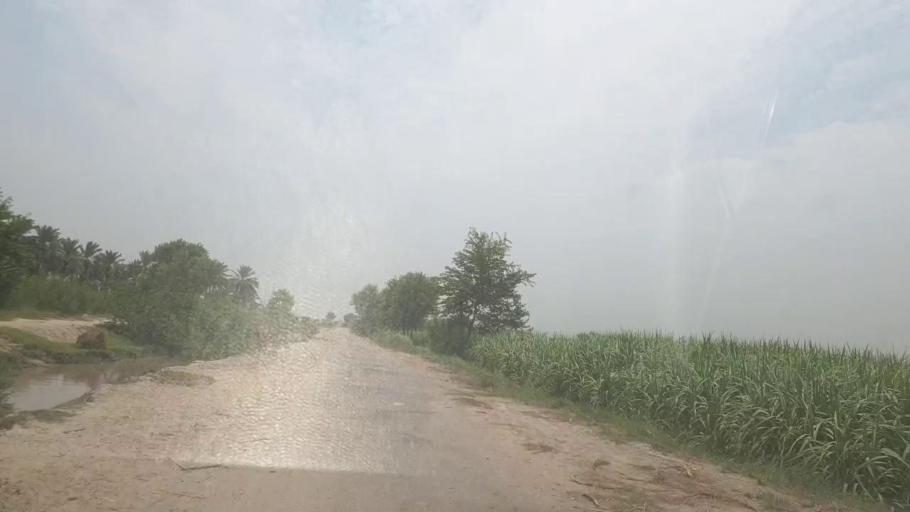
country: PK
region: Sindh
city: Kot Diji
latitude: 27.4261
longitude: 68.6497
